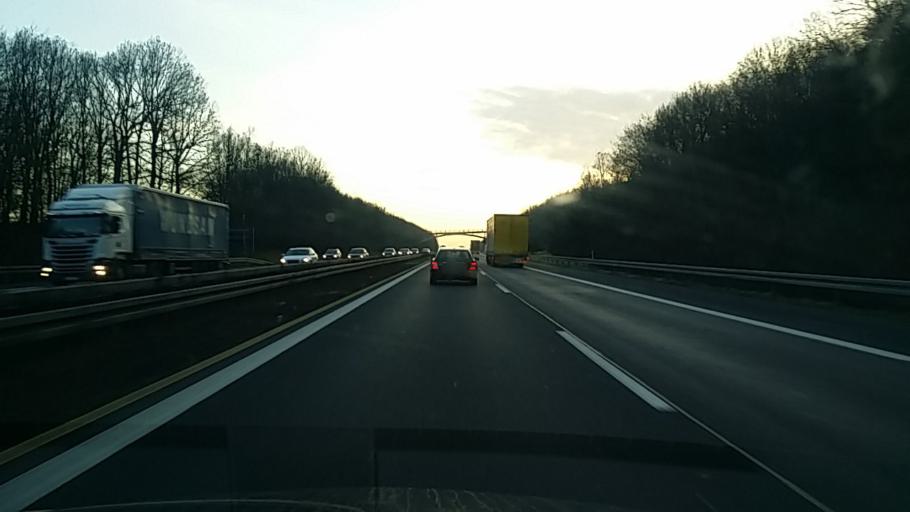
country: DE
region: Bavaria
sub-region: Regierungsbezirk Unterfranken
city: Unterpleichfeld
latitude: 49.8869
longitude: 9.9984
